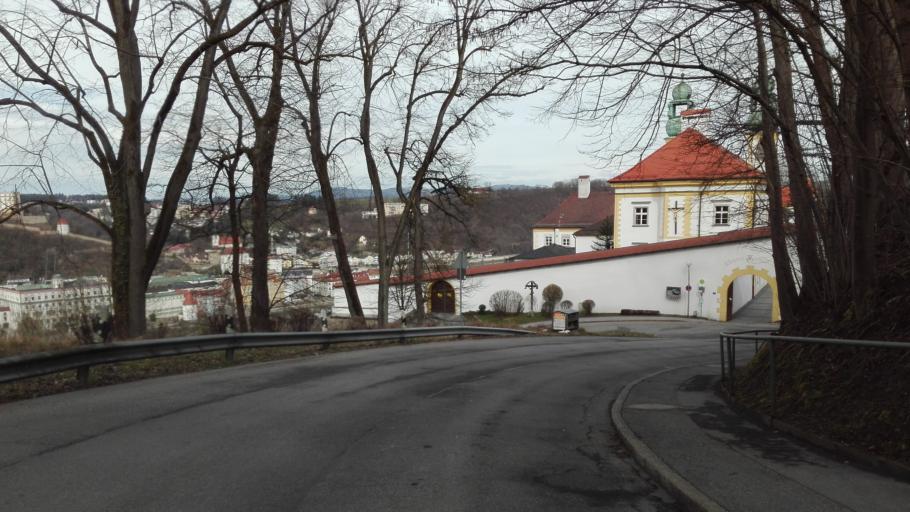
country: DE
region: Bavaria
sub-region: Lower Bavaria
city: Passau
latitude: 48.5685
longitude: 13.4685
